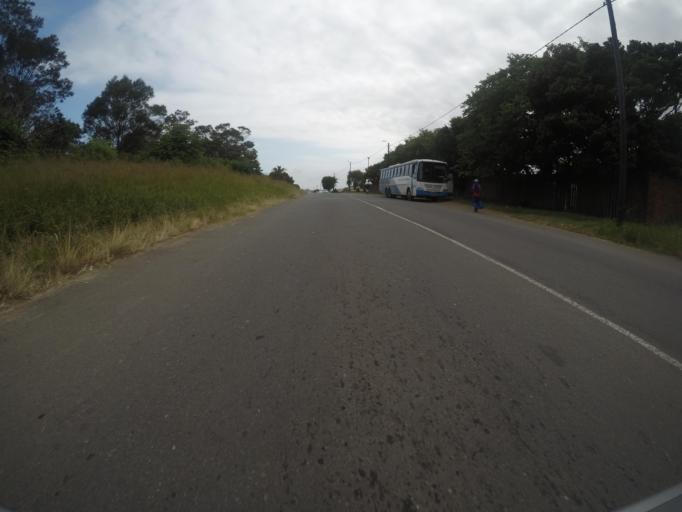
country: ZA
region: Eastern Cape
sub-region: Buffalo City Metropolitan Municipality
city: East London
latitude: -32.9917
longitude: 27.8878
